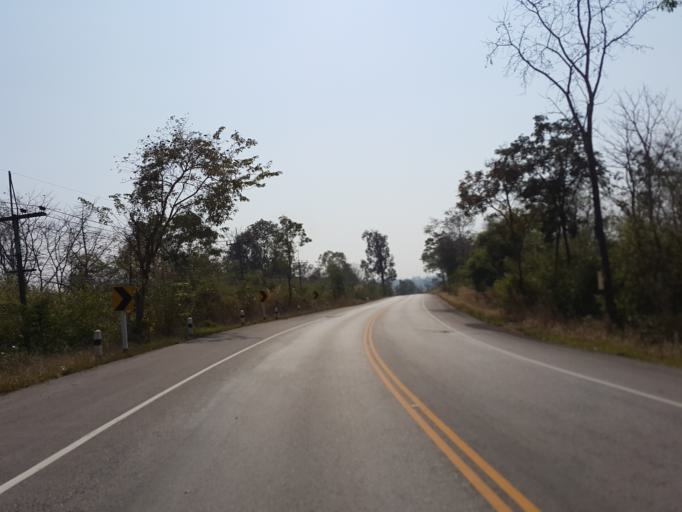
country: TH
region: Lampang
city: Mueang Pan
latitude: 18.8730
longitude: 99.5992
